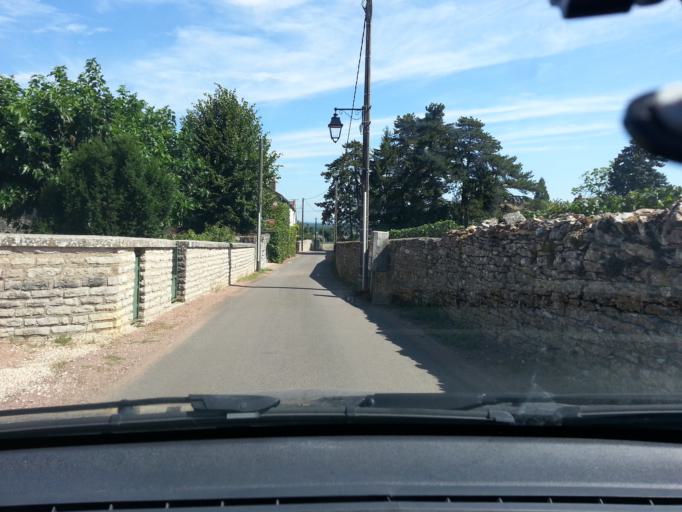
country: FR
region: Bourgogne
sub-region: Departement de Saone-et-Loire
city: Givry
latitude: 46.7745
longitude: 4.7230
